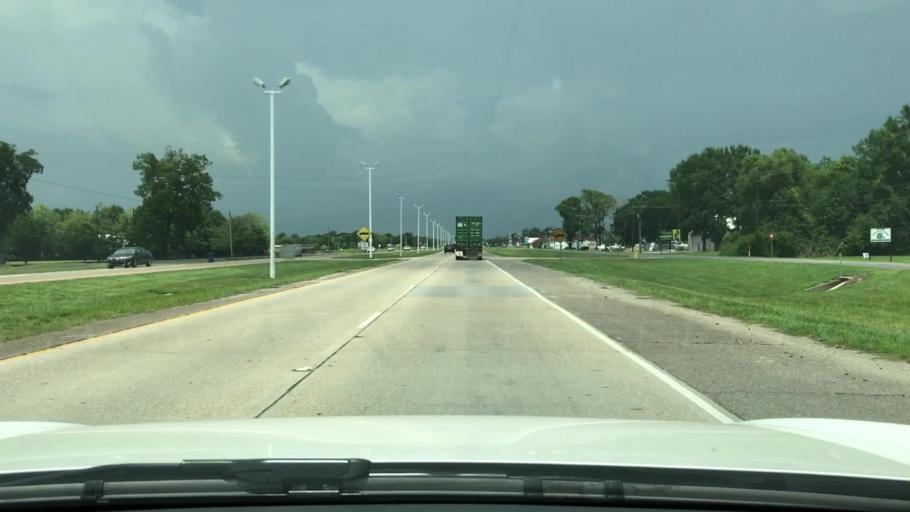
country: US
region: Louisiana
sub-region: West Baton Rouge Parish
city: Addis
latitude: 30.3688
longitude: -91.2579
